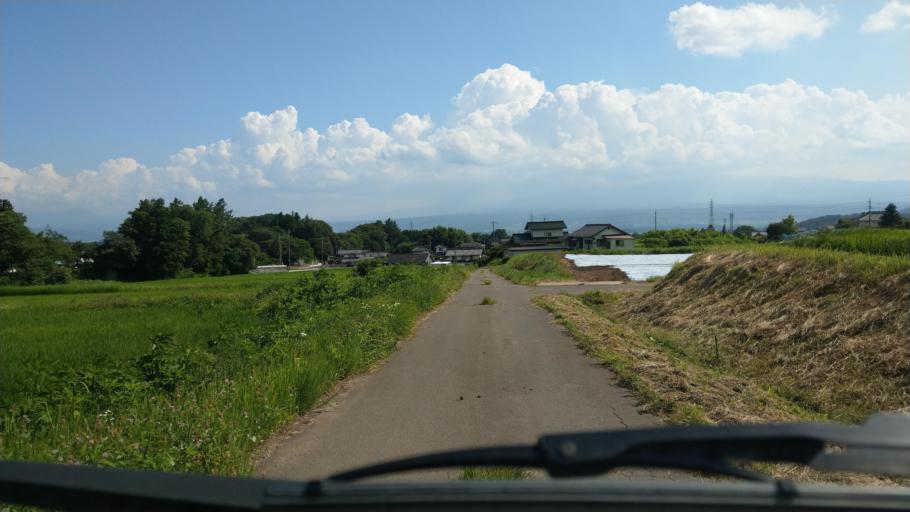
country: JP
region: Nagano
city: Komoro
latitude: 36.3249
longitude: 138.4499
